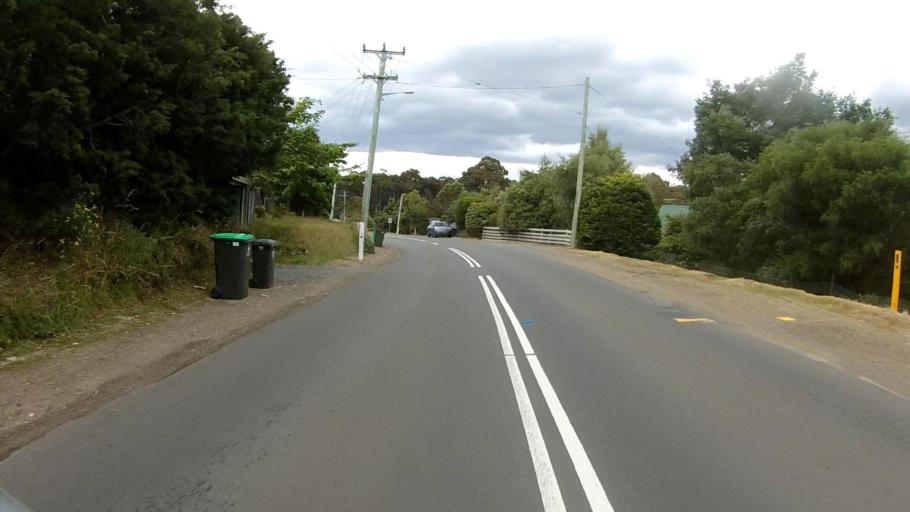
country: AU
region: Tasmania
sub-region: Hobart
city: Dynnyrne
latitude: -42.9144
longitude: 147.2675
